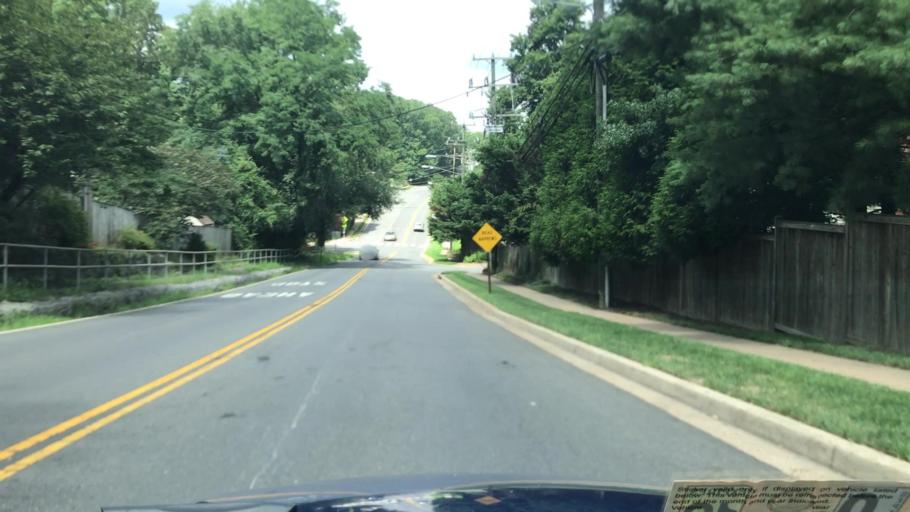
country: US
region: Virginia
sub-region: Fairfax County
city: Vienna
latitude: 38.9053
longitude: -77.2771
